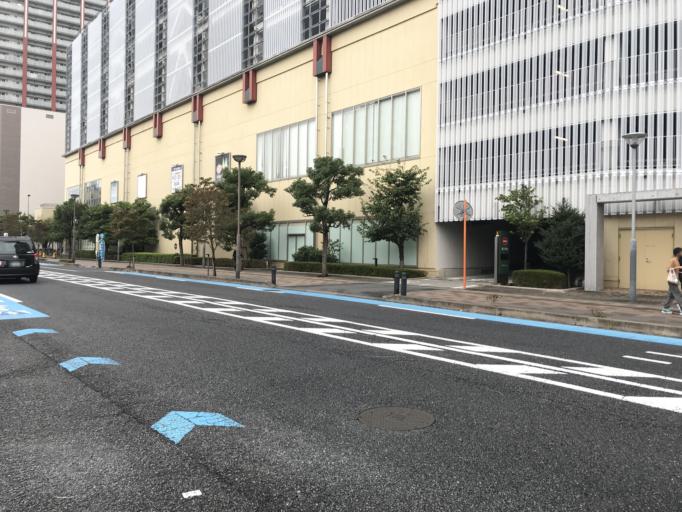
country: JP
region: Saitama
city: Yono
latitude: 35.8424
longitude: 139.6460
